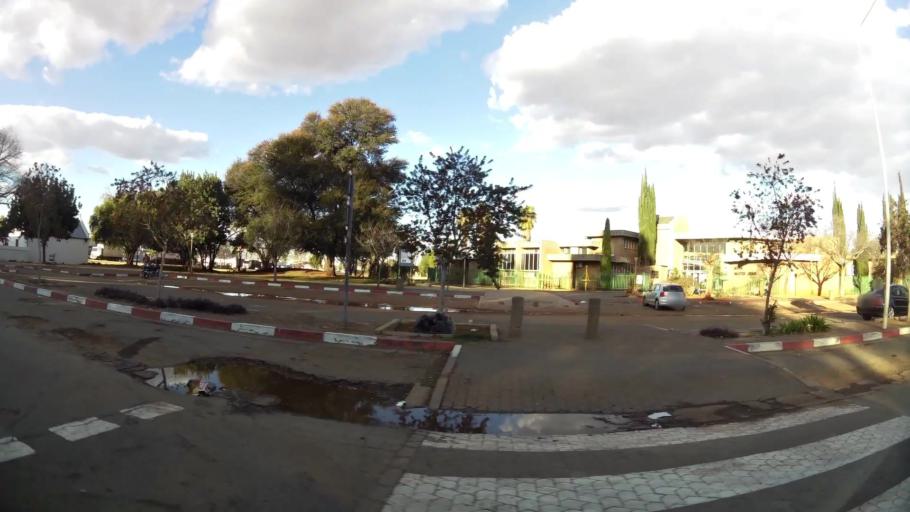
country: ZA
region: North-West
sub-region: Dr Kenneth Kaunda District Municipality
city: Potchefstroom
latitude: -26.7155
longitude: 27.0992
